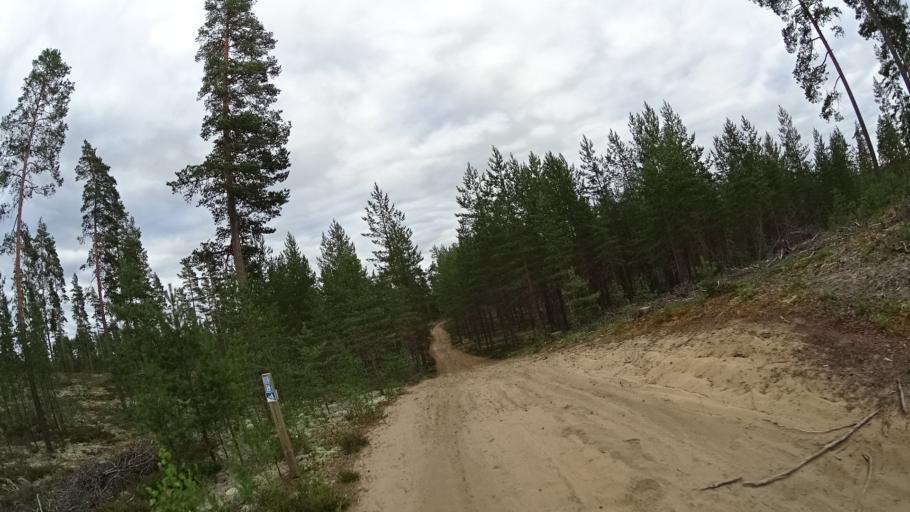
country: FI
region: Satakunta
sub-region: Pohjois-Satakunta
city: Jaemijaervi
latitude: 61.7609
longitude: 22.7784
